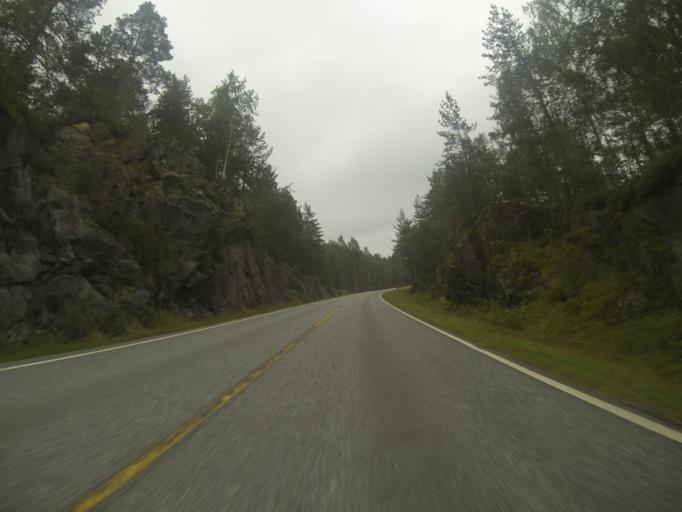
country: NO
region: Rogaland
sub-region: Suldal
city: Sand
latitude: 59.5192
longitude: 6.2368
